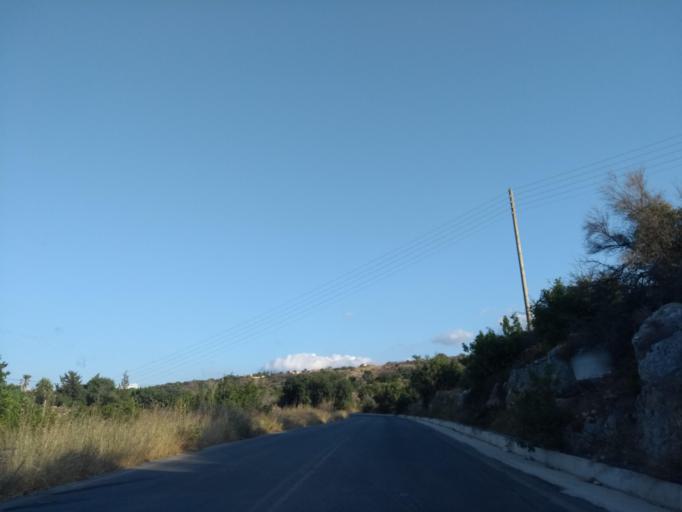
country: GR
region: Crete
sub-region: Nomos Chanias
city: Kalivai
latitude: 35.4278
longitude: 24.1808
